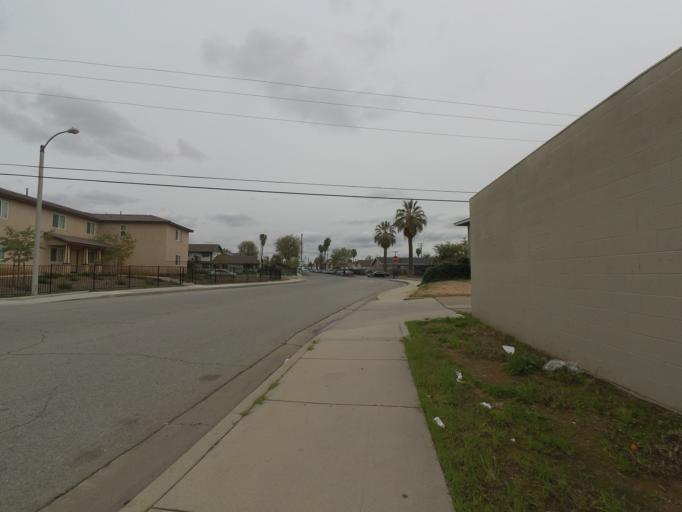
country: US
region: California
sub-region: Riverside County
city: March Air Force Base
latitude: 33.9182
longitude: -117.2659
